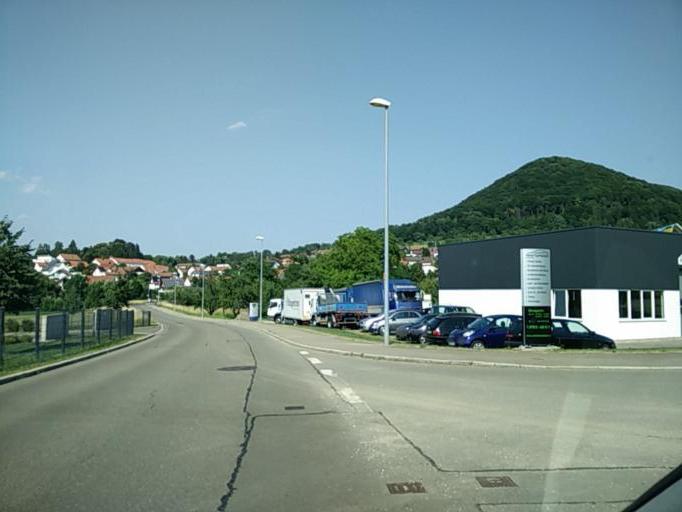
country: DE
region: Baden-Wuerttemberg
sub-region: Tuebingen Region
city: Gomaringen
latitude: 48.4370
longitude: 9.1426
